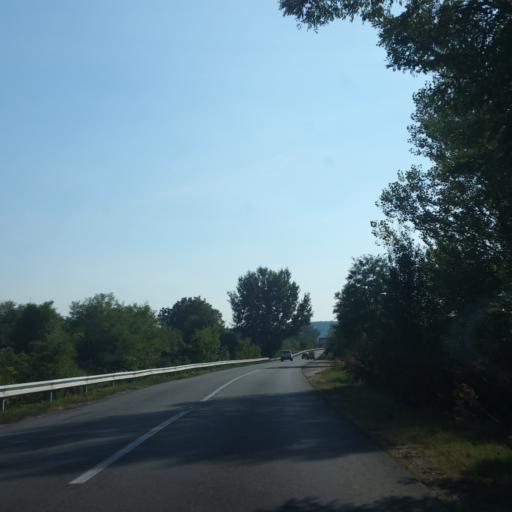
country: RO
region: Arges
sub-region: Comuna Merisani
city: Merisani
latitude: 44.9775
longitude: 24.7496
